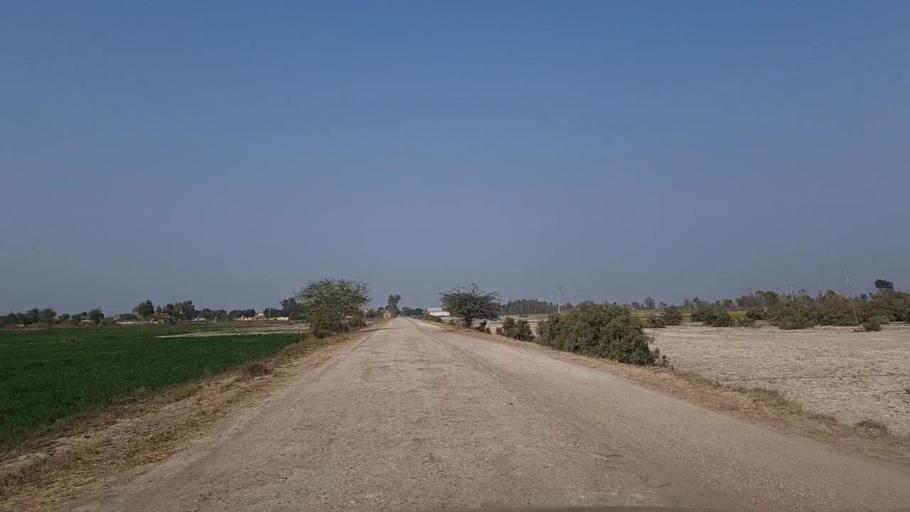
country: PK
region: Sindh
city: Daur
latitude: 26.4217
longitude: 68.4089
